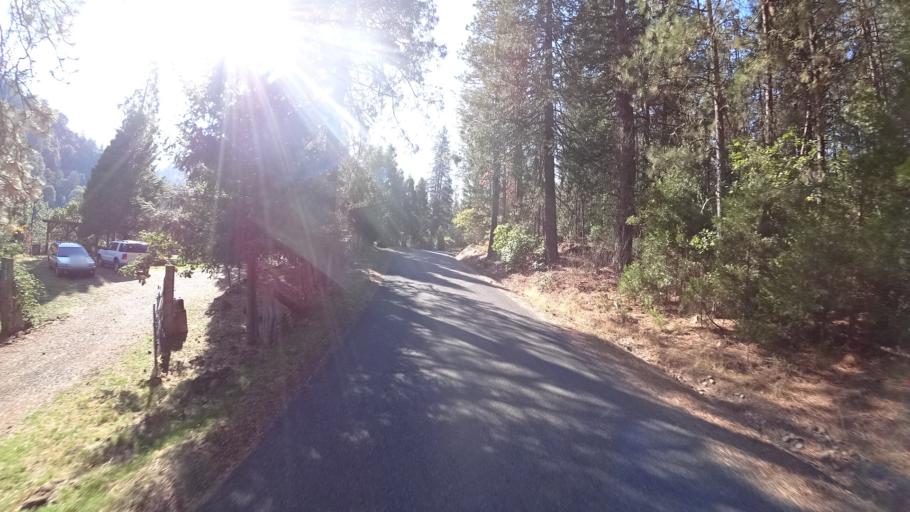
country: US
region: California
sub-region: Siskiyou County
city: Yreka
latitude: 41.7391
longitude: -123.0041
